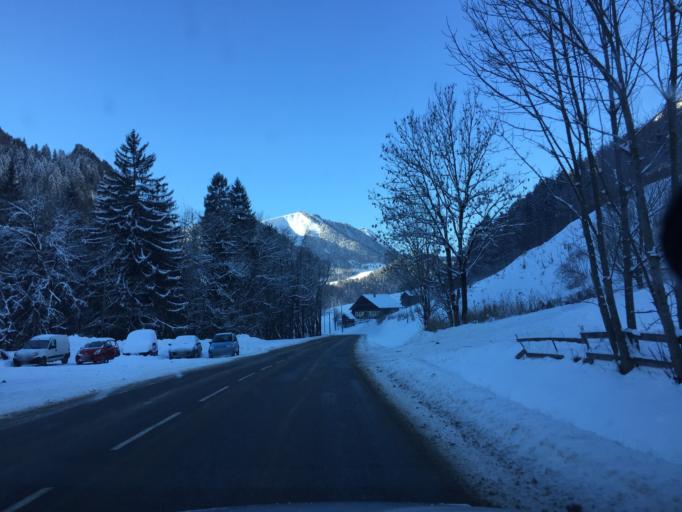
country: FR
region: Rhone-Alpes
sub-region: Departement de la Haute-Savoie
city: Abondance
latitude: 46.2851
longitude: 6.7377
